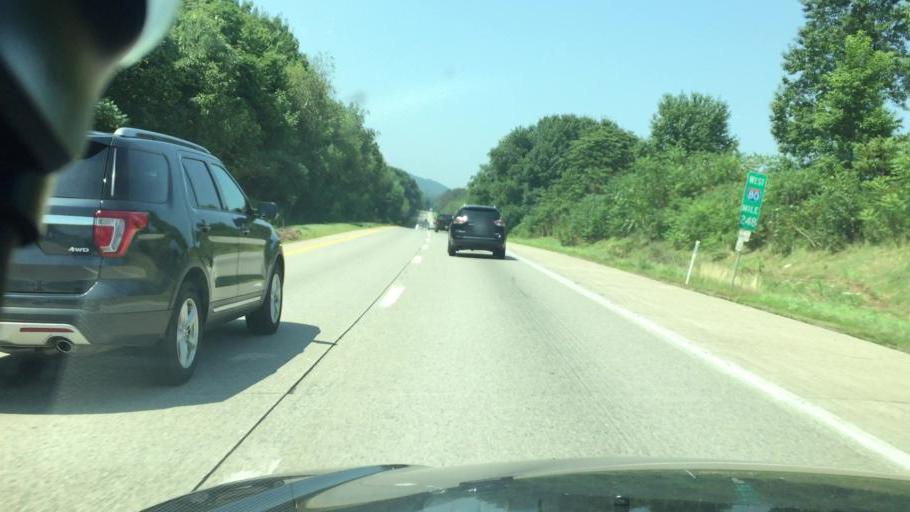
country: US
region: Pennsylvania
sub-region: Luzerne County
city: Nescopeck
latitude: 41.0169
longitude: -76.2091
